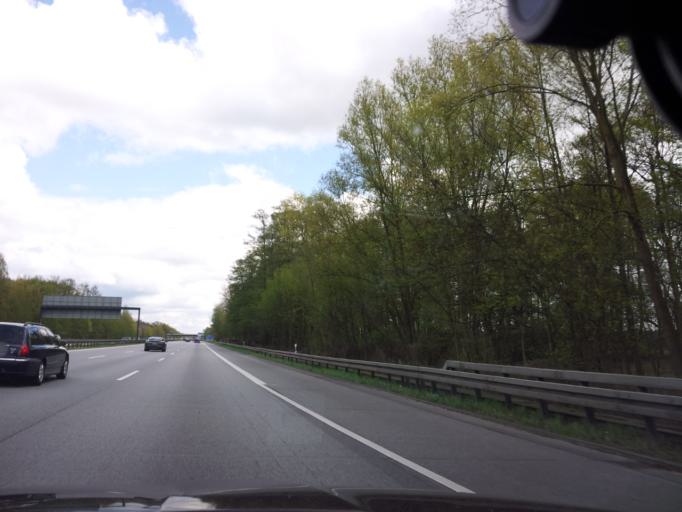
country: DE
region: Brandenburg
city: Rangsdorf
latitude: 52.3098
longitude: 13.4614
